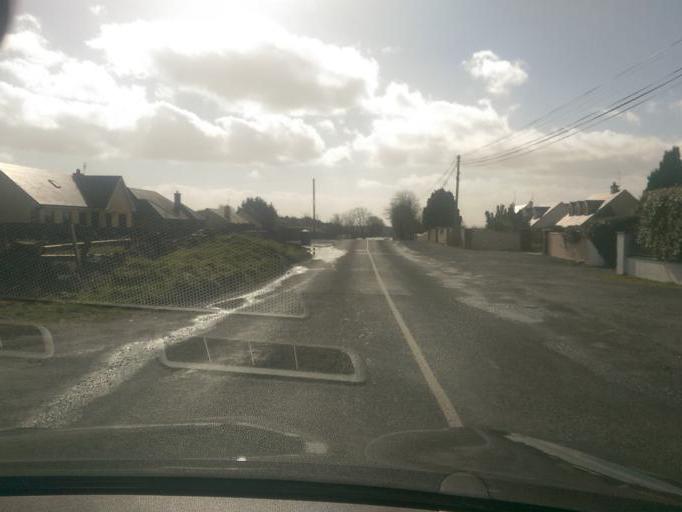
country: IE
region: Connaught
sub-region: County Galway
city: Athenry
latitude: 53.3480
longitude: -8.7086
